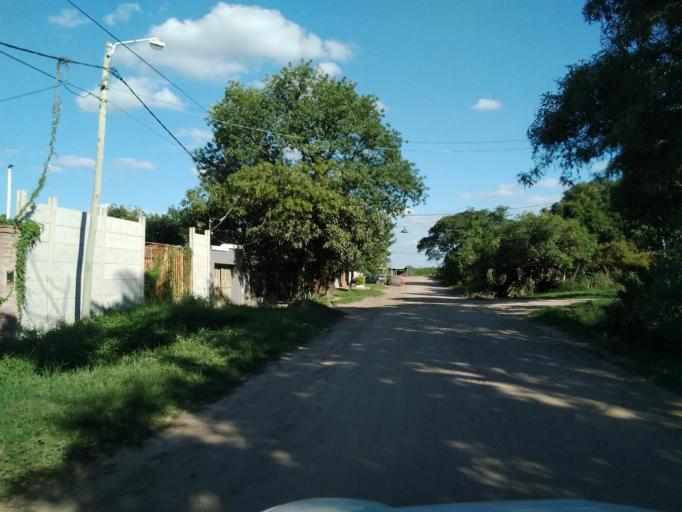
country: AR
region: Corrientes
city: Corrientes
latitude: -27.4623
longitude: -58.7767
